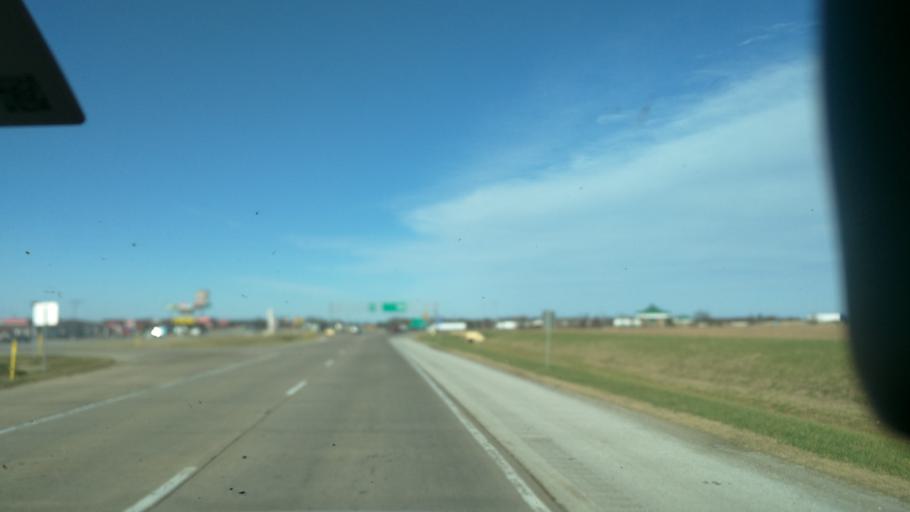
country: US
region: Oklahoma
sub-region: Craig County
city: Vinita
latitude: 36.5635
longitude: -95.2200
